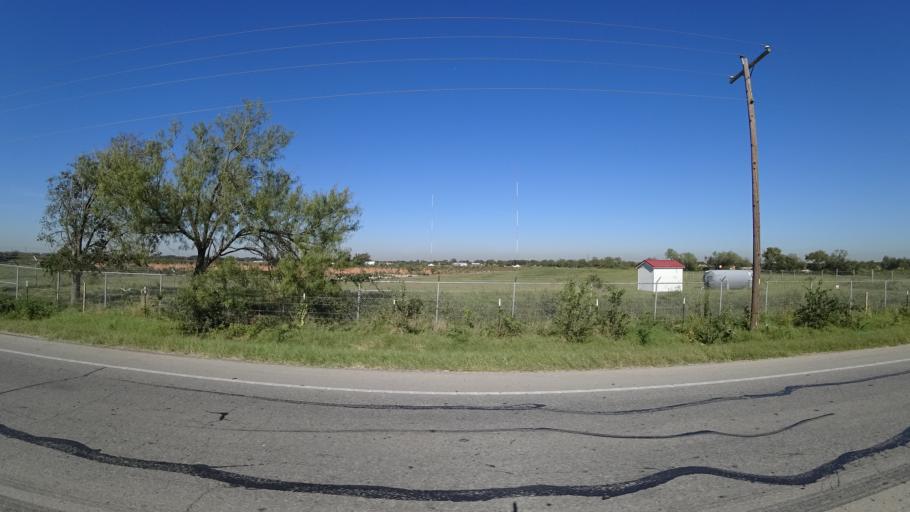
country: US
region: Texas
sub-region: Travis County
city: Hornsby Bend
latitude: 30.2363
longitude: -97.6249
